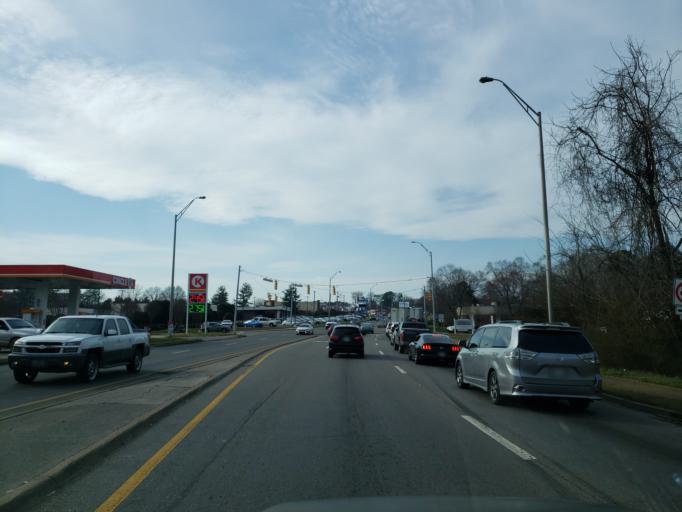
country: US
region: Tennessee
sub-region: Bradley County
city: East Cleveland
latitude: 35.1764
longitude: -84.8615
